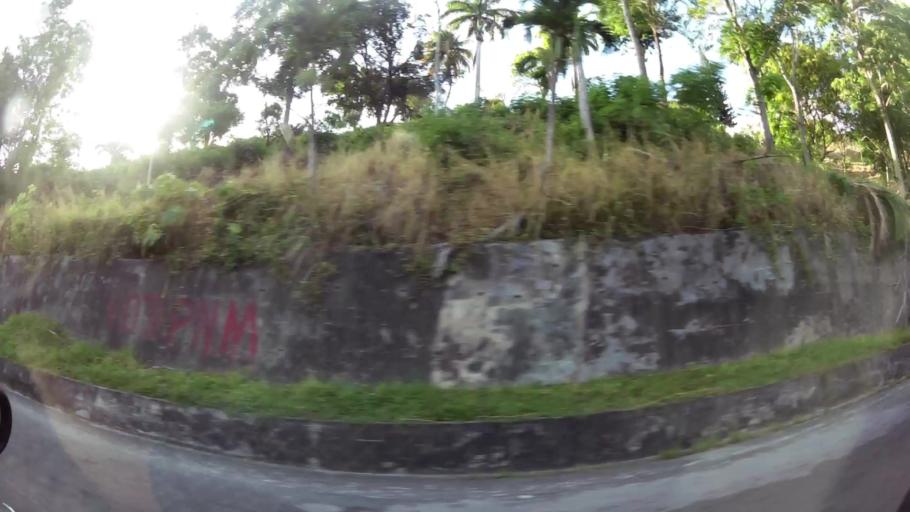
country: TT
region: Eastern Tobago
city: Roxborough
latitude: 11.2288
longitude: -60.6093
